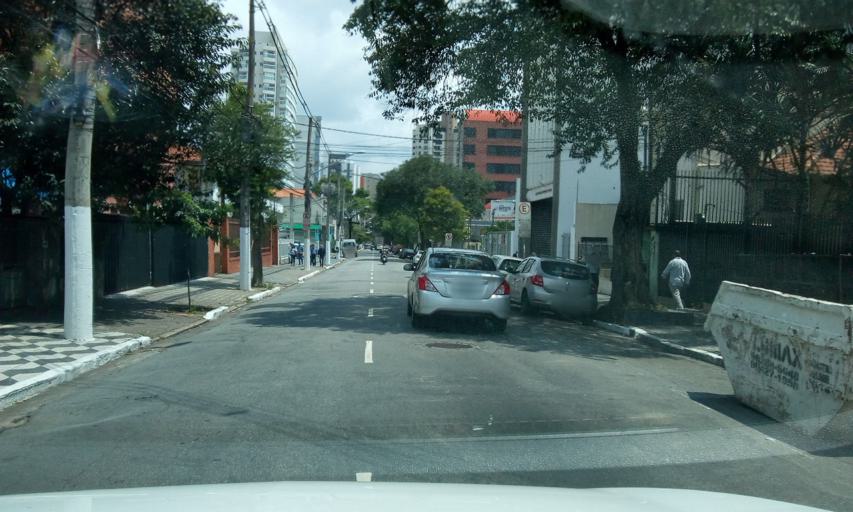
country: BR
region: Sao Paulo
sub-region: Sao Paulo
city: Sao Paulo
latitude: -23.5846
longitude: -46.6383
